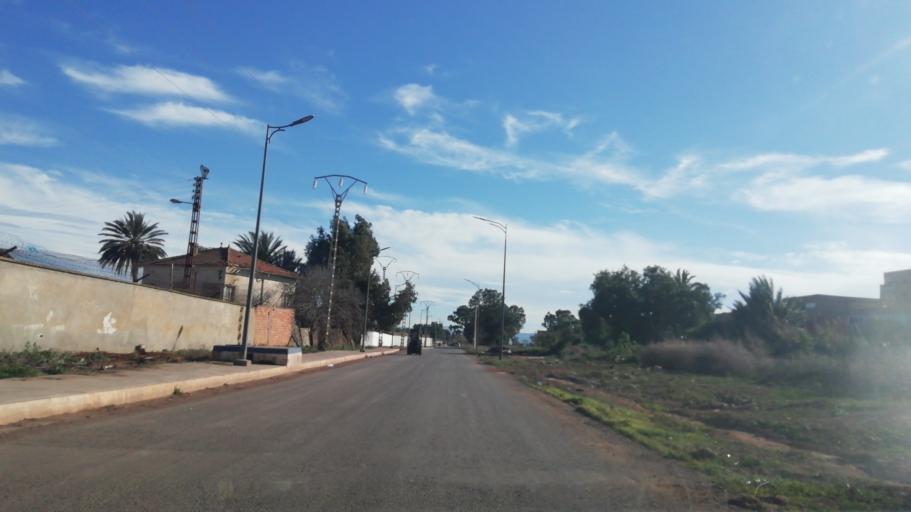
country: DZ
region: Oran
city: Es Senia
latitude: 35.6198
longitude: -0.5865
